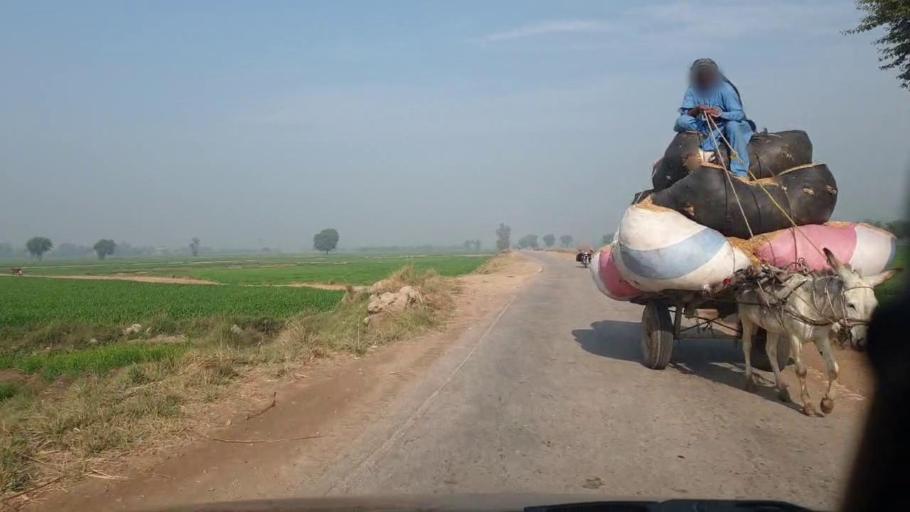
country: PK
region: Sindh
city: Shahdadpur
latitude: 25.9590
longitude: 68.5871
